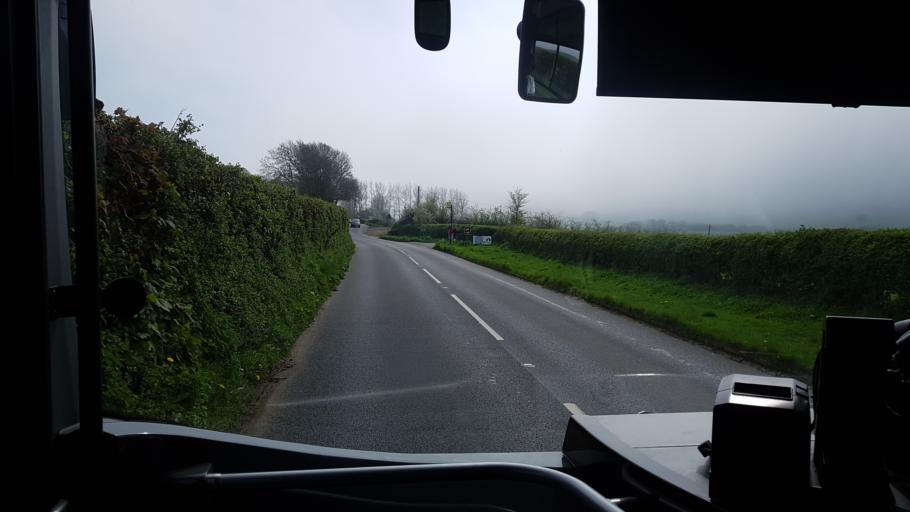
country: GB
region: England
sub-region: Isle of Wight
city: Ventnor
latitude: 50.6267
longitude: -1.2233
